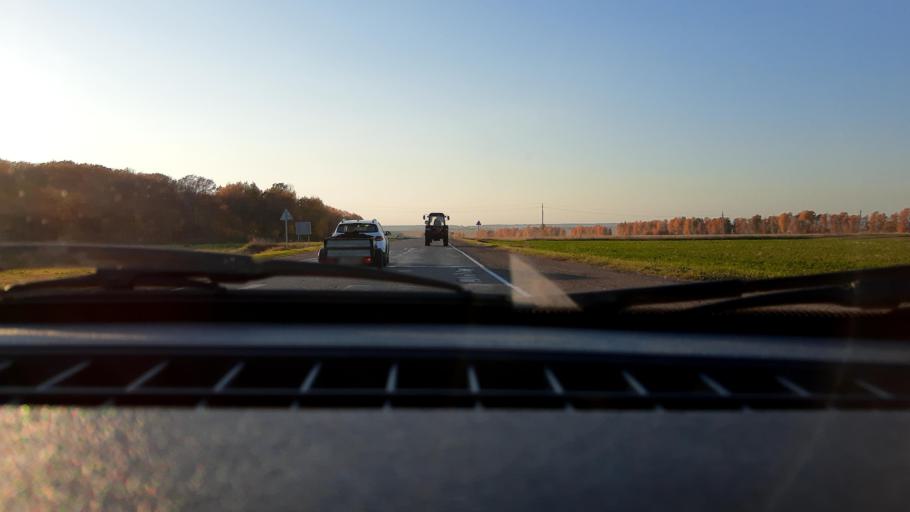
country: RU
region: Bashkortostan
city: Asanovo
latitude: 54.8255
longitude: 55.6449
